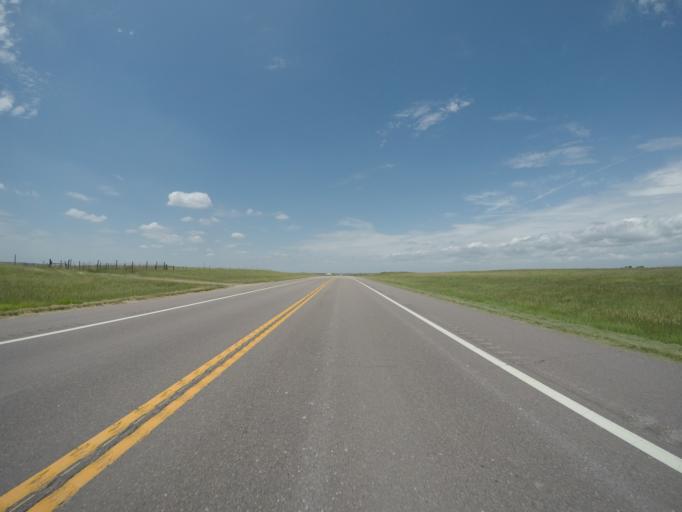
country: US
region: Kansas
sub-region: Graham County
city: Hill City
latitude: 39.3793
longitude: -99.7237
